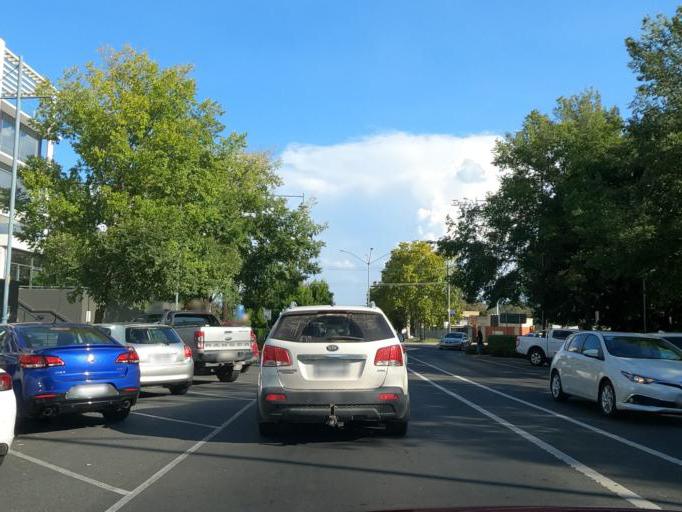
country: AU
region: New South Wales
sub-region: Albury Municipality
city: South Albury
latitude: -36.0816
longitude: 146.9104
